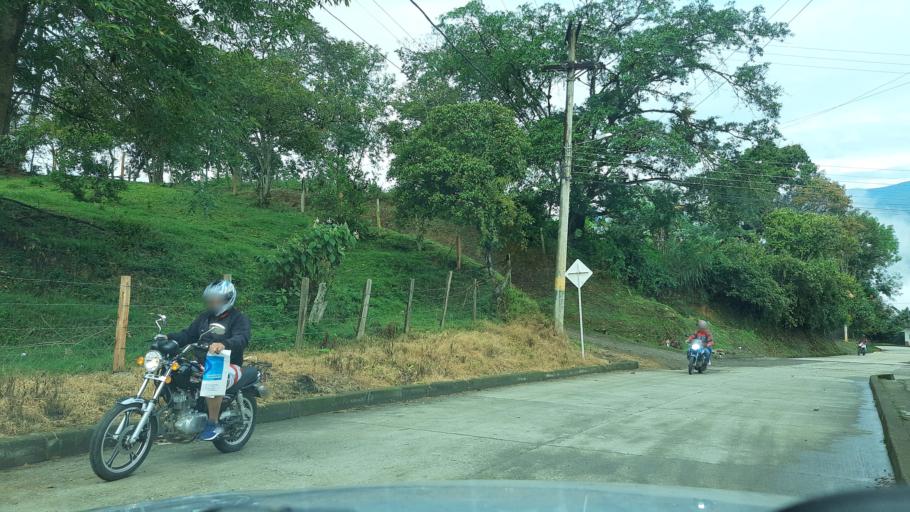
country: CO
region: Boyaca
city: Garagoa
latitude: 5.0790
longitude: -73.3654
